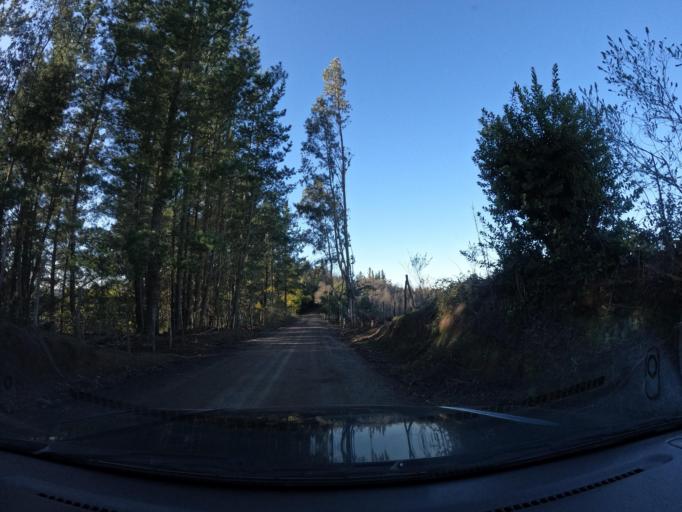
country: CL
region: Biobio
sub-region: Provincia de Concepcion
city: Chiguayante
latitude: -37.0135
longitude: -72.8614
